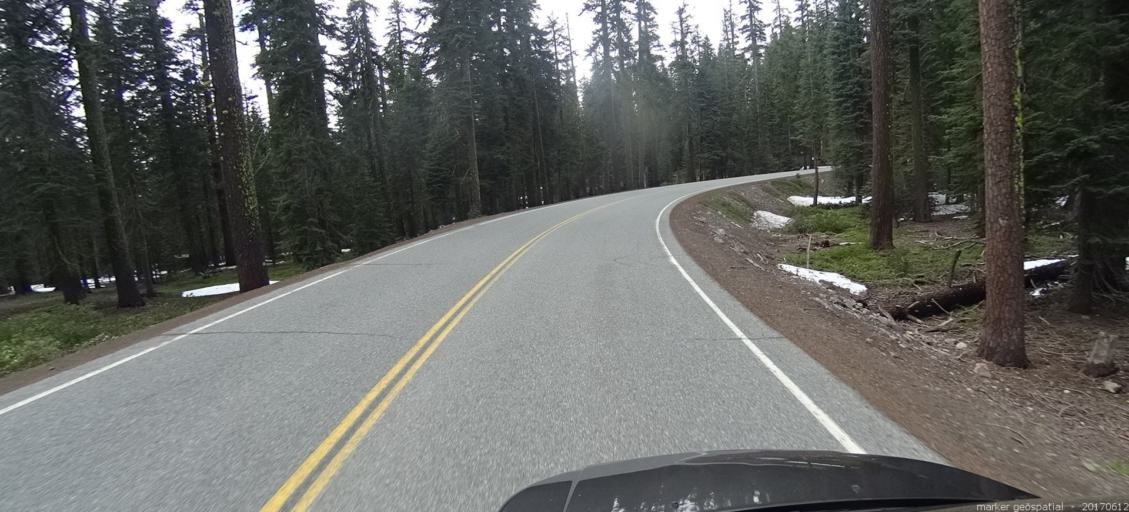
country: US
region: California
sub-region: Siskiyou County
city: Mount Shasta
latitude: 41.3440
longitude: -122.2530
